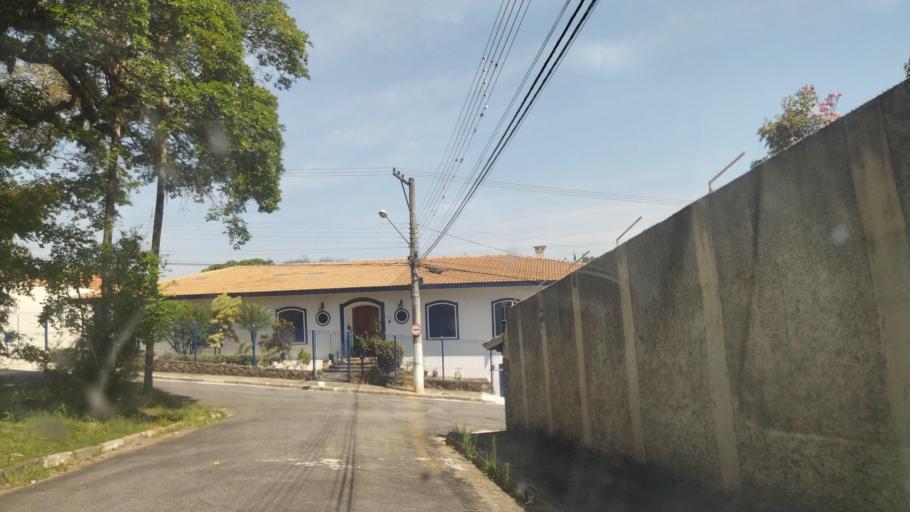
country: BR
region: Sao Paulo
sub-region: Atibaia
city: Atibaia
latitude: -23.1221
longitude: -46.5496
